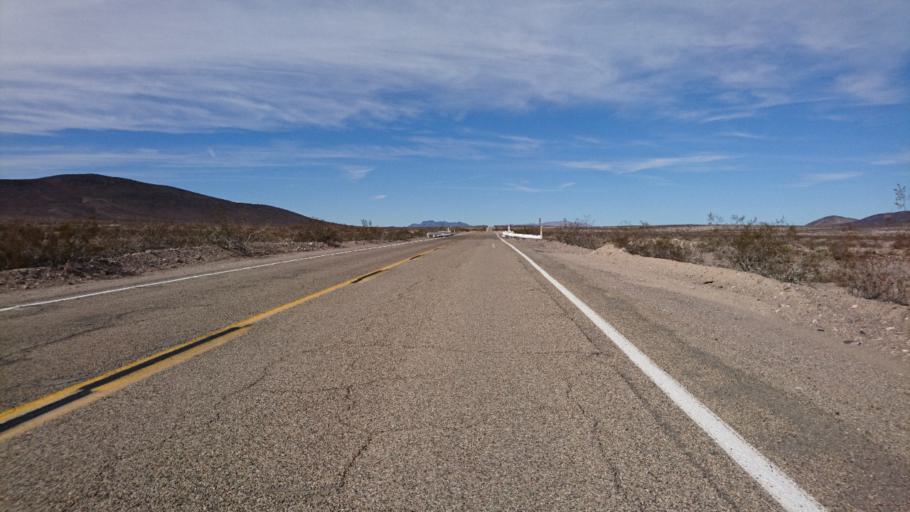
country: US
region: California
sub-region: San Bernardino County
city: Twentynine Palms
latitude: 34.6947
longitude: -116.0527
